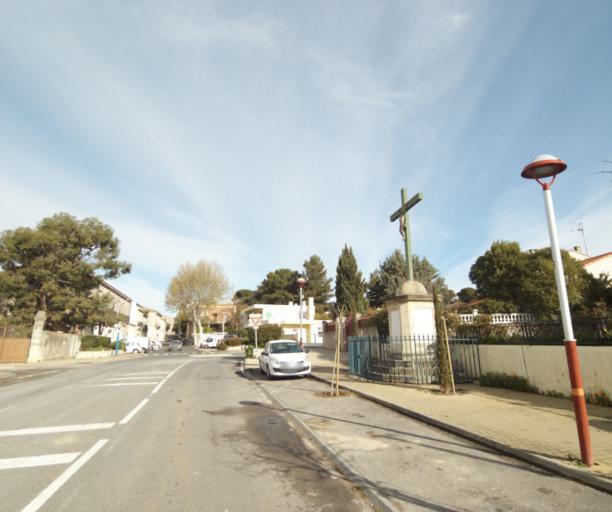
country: FR
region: Languedoc-Roussillon
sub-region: Departement de l'Herault
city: Saint-Jean-de-Vedas
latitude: 43.5761
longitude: 3.8287
